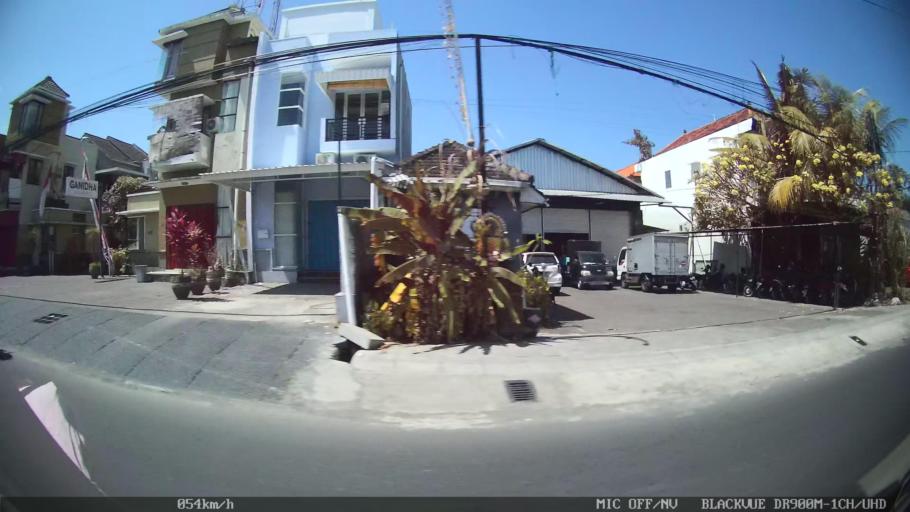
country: ID
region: Bali
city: Denpasar
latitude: -8.6682
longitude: 115.1777
